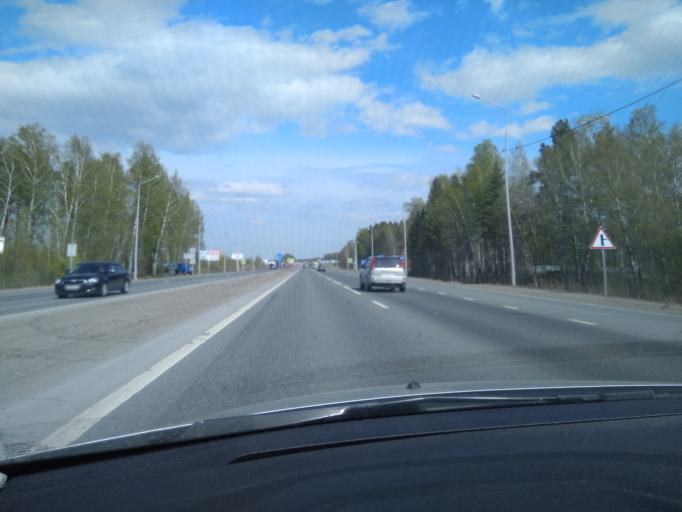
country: RU
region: Tjumen
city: Moskovskiy
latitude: 57.1155
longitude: 65.4215
